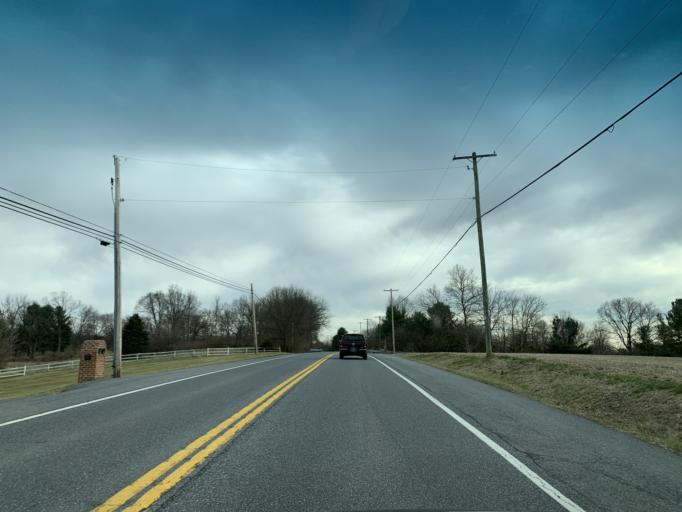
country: US
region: Maryland
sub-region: Washington County
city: Robinwood
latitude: 39.5887
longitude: -77.6978
